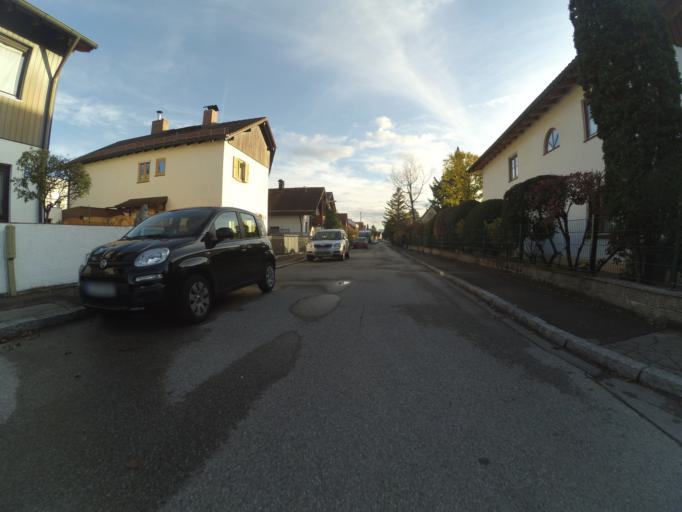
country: DE
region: Bavaria
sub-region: Upper Bavaria
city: Bogenhausen
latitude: 48.1965
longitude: 11.5885
